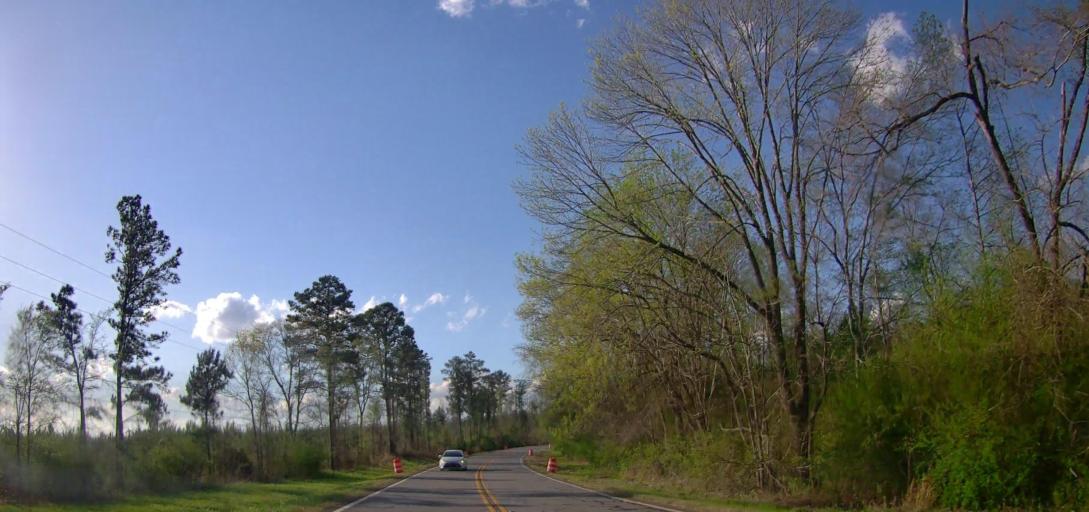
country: US
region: Georgia
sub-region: Baldwin County
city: Milledgeville
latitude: 33.1094
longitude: -83.2834
